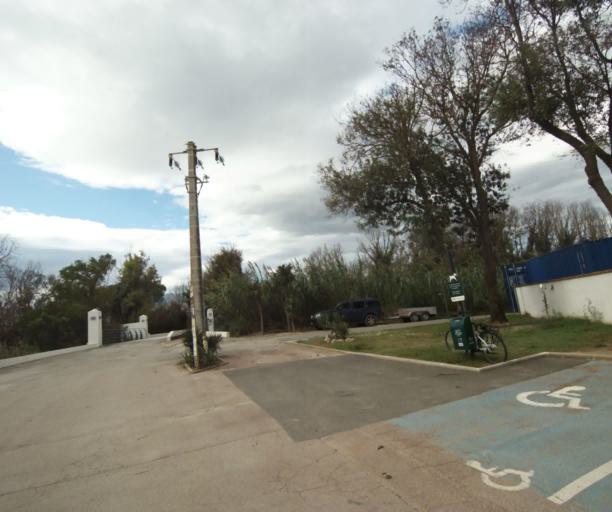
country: FR
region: Languedoc-Roussillon
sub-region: Departement des Pyrenees-Orientales
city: Argelers
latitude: 42.5756
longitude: 3.0423
